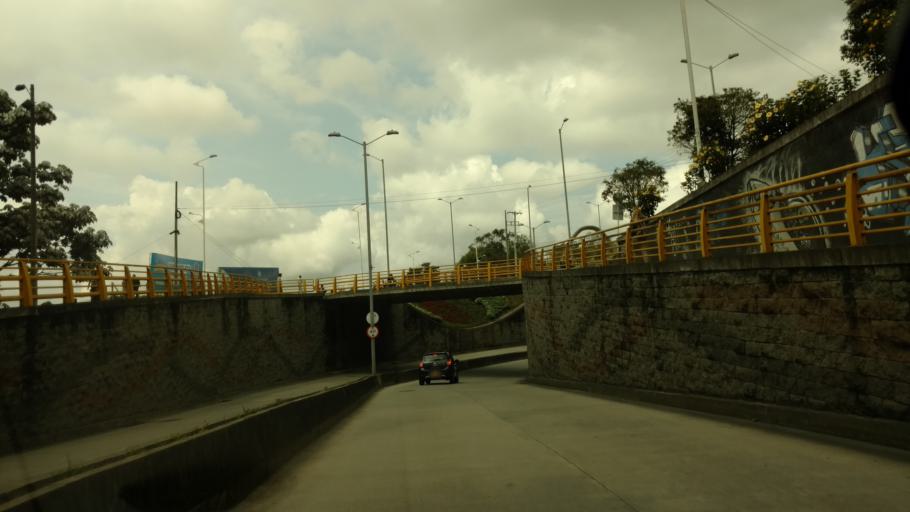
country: CO
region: Caldas
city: Villamaria
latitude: 5.0555
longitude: -75.4899
